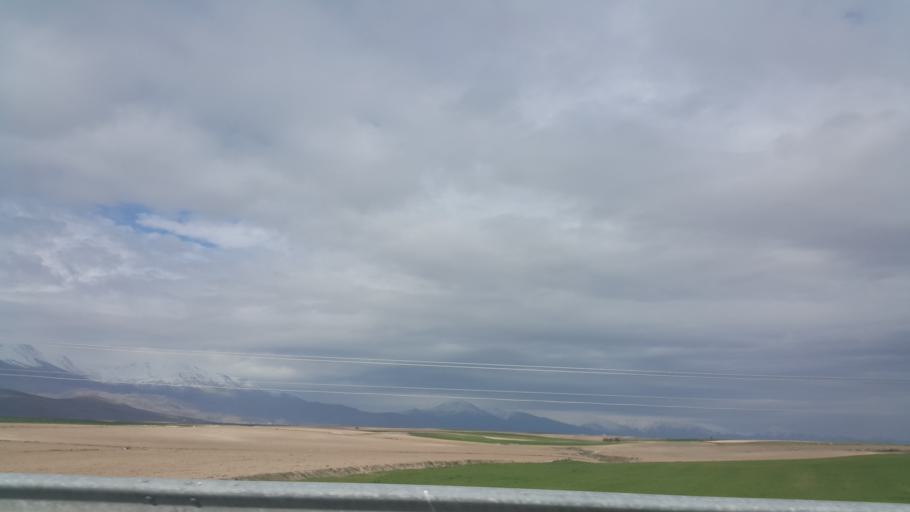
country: TR
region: Aksaray
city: Taspinar
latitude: 37.9983
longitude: 34.0622
